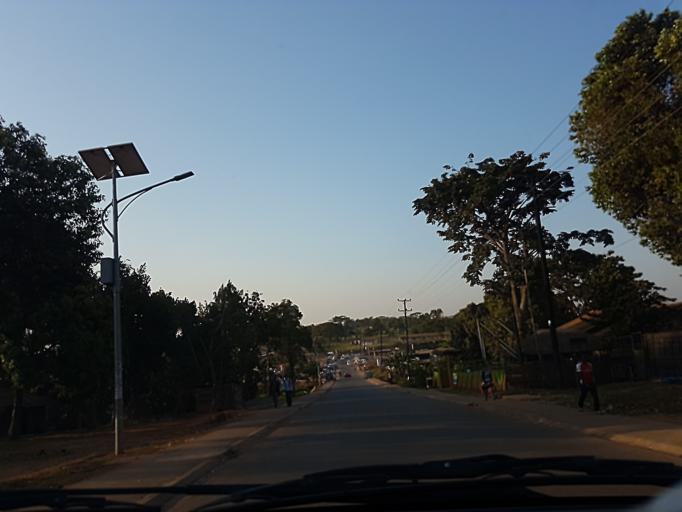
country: UG
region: Central Region
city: Kampala Central Division
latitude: 0.4026
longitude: 32.5892
